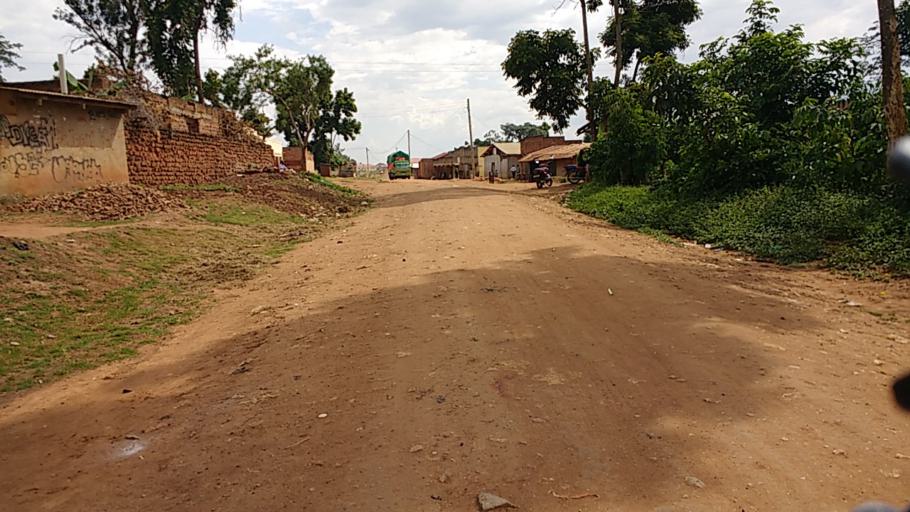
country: UG
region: Eastern Region
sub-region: Mbale District
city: Mbale
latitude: 1.0872
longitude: 34.1654
